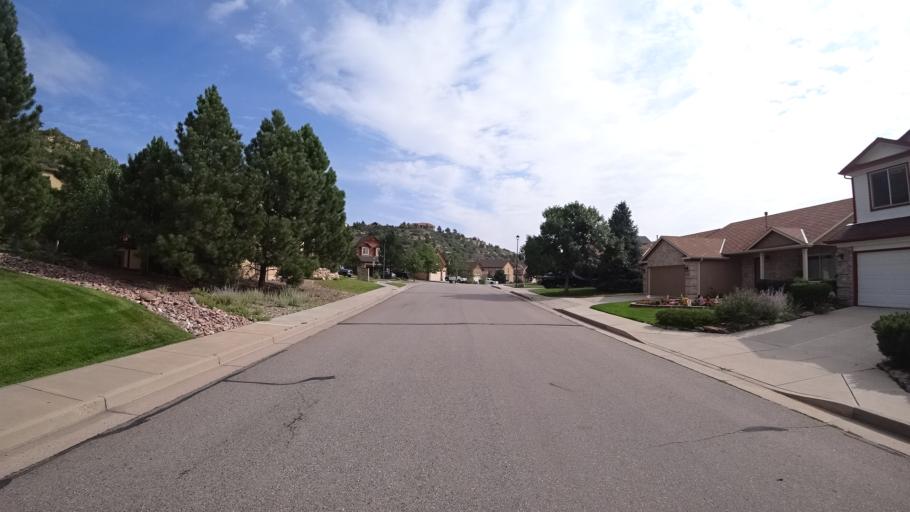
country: US
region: Colorado
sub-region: El Paso County
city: Colorado Springs
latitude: 38.8942
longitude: -104.7886
